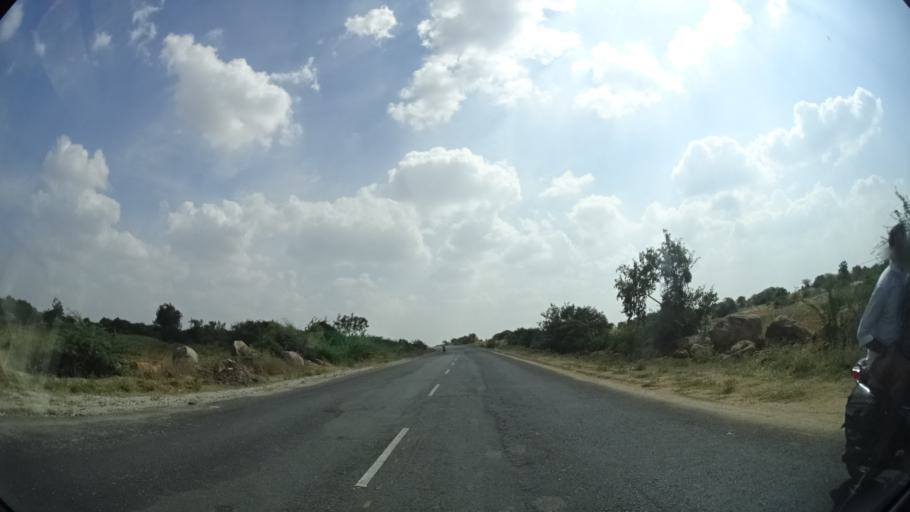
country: IN
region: Andhra Pradesh
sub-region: Anantapur
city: Uravakonda
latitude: 14.8227
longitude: 77.3424
